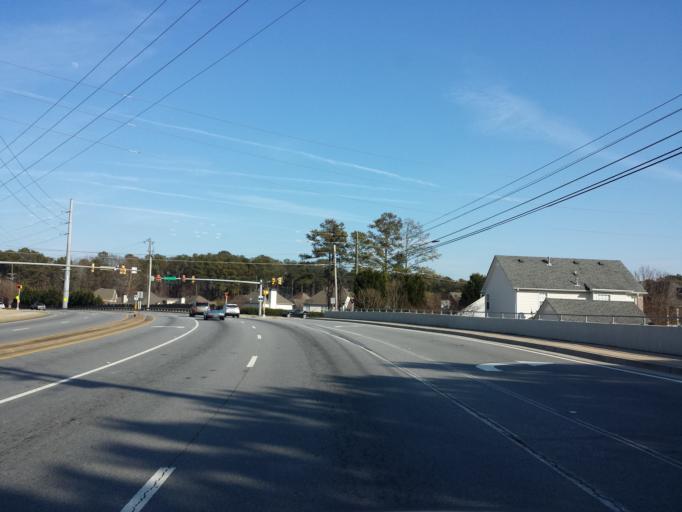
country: US
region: Georgia
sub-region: Cobb County
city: Kennesaw
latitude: 34.0340
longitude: -84.5513
